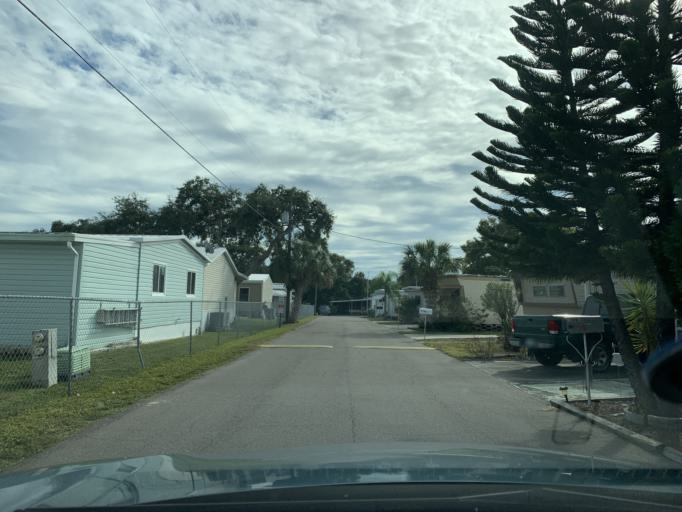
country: US
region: Florida
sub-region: Pinellas County
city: Kenneth City
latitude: 27.8118
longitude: -82.7348
